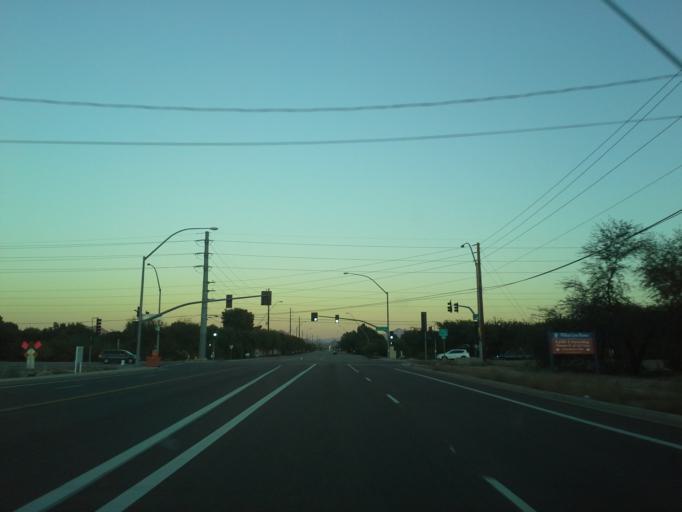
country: US
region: Arizona
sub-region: Maricopa County
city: Mesa
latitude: 33.4663
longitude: -111.7542
